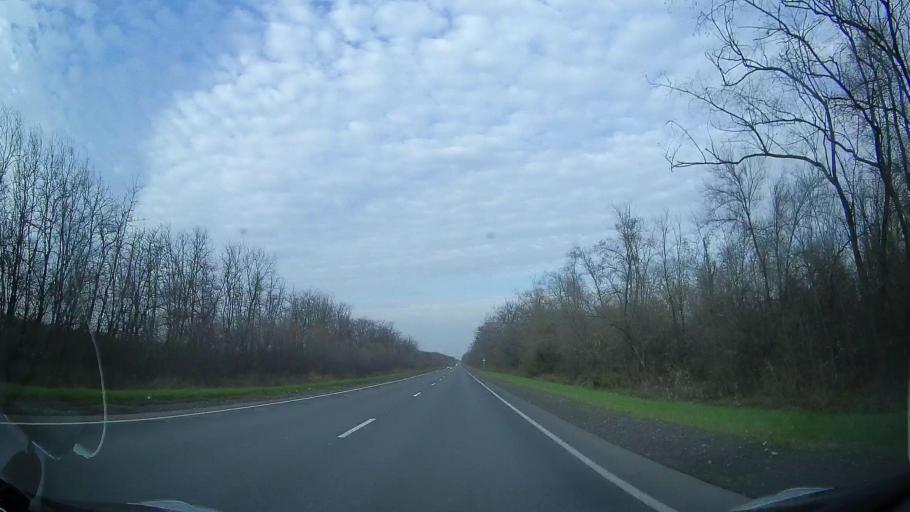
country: RU
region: Rostov
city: Bagayevskaya
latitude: 47.1095
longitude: 40.2767
